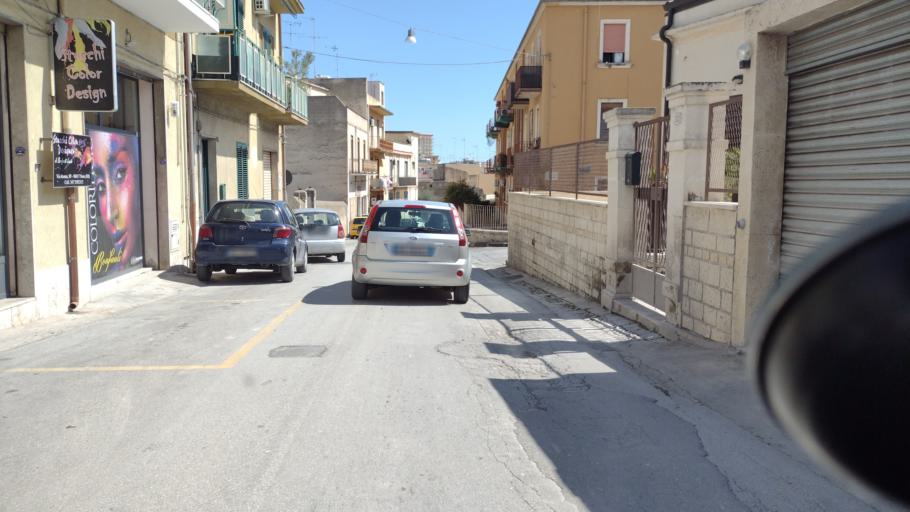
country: IT
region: Sicily
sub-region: Provincia di Siracusa
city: Noto
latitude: 36.8891
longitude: 15.0690
